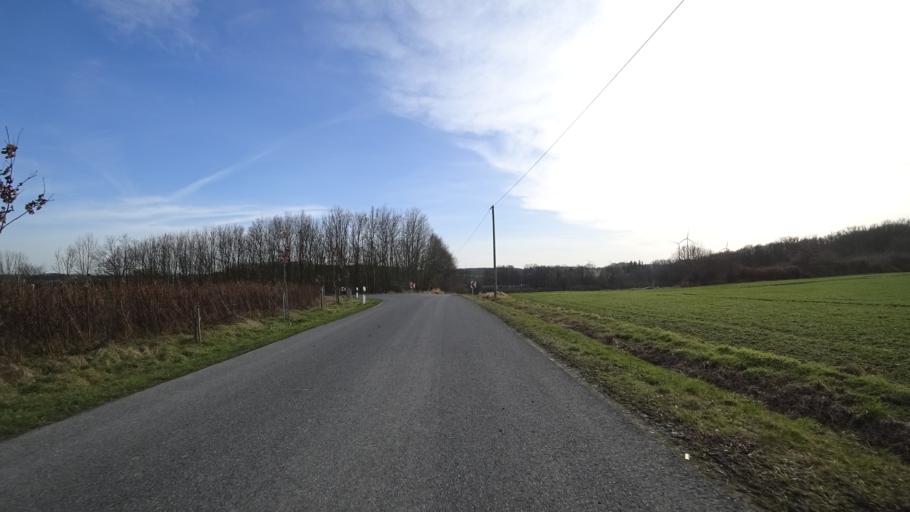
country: DE
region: North Rhine-Westphalia
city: Oelde
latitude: 51.8081
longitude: 8.1105
